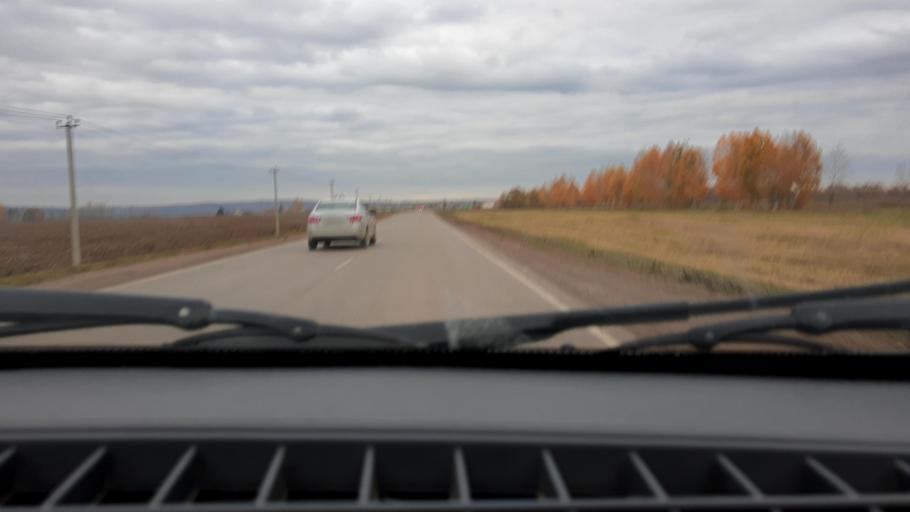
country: RU
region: Bashkortostan
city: Kabakovo
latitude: 54.5440
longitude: 56.0809
